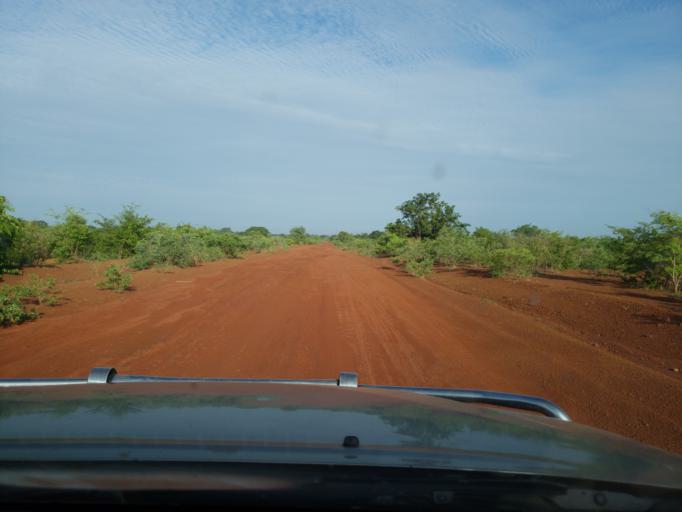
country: ML
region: Sikasso
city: Koutiala
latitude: 12.4260
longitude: -5.6452
